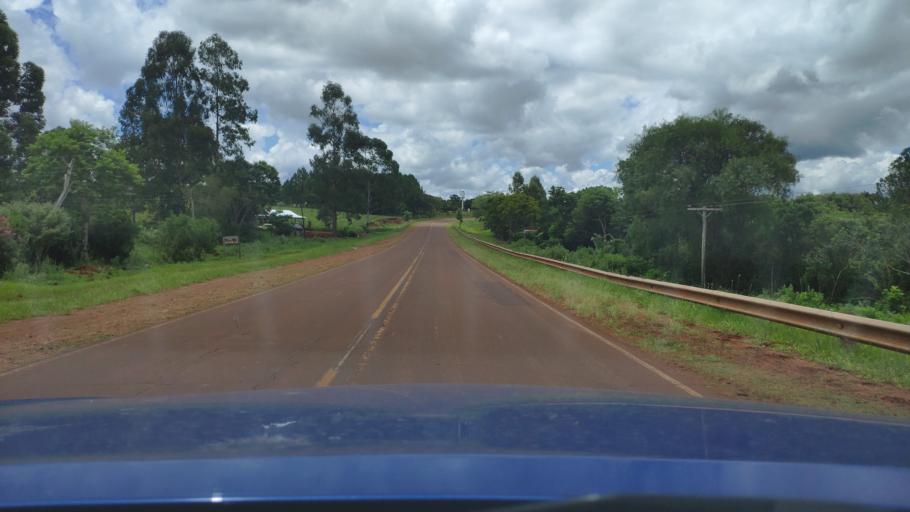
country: AR
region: Misiones
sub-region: Departamento de San Javier
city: San Javier
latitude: -27.8589
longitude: -55.2530
